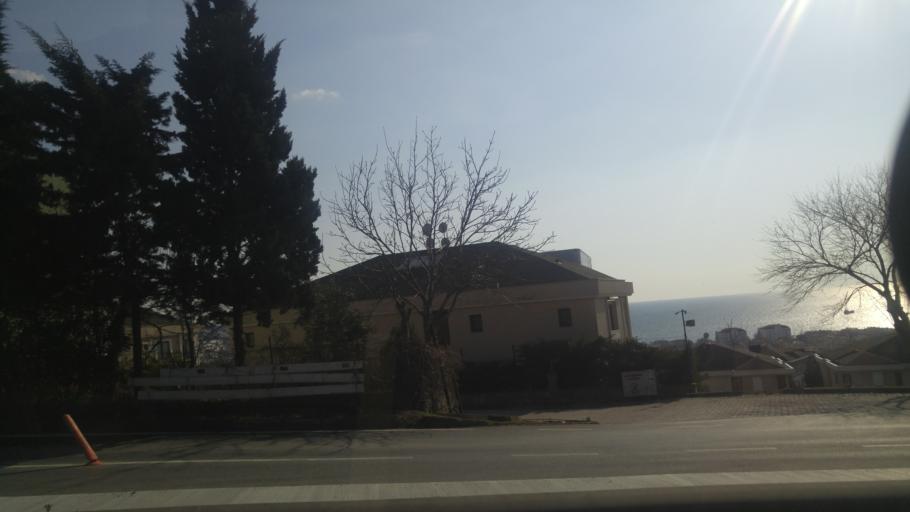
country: TR
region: Istanbul
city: Bueyuekcekmece
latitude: 41.0237
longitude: 28.5964
